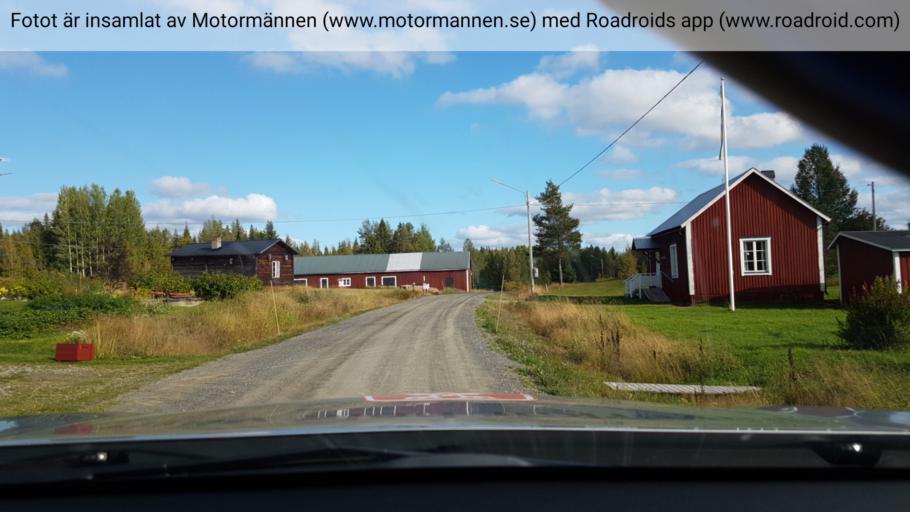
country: SE
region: Vaesterbotten
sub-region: Sorsele Kommun
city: Sorsele
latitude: 65.4638
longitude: 17.7659
